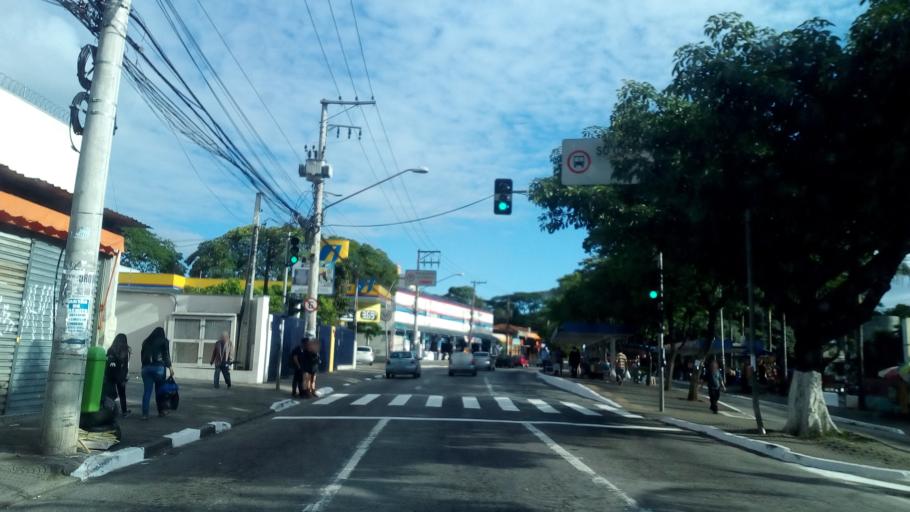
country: BR
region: Sao Paulo
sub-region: Guarulhos
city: Guarulhos
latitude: -23.4641
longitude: -46.5317
